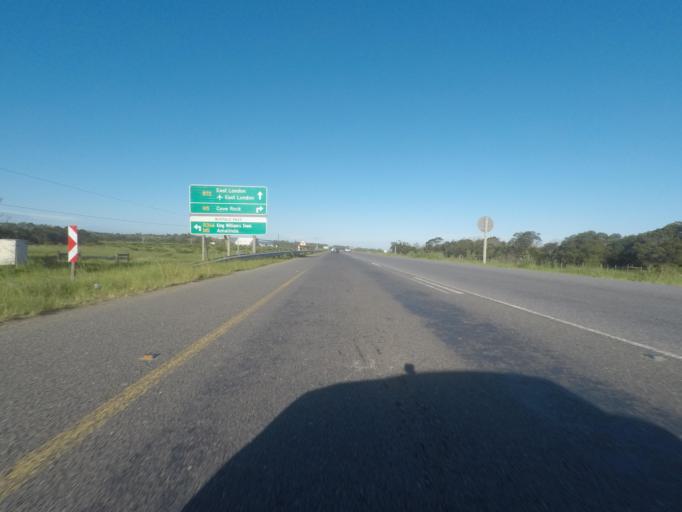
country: ZA
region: Eastern Cape
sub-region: Buffalo City Metropolitan Municipality
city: East London
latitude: -33.0538
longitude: 27.8057
